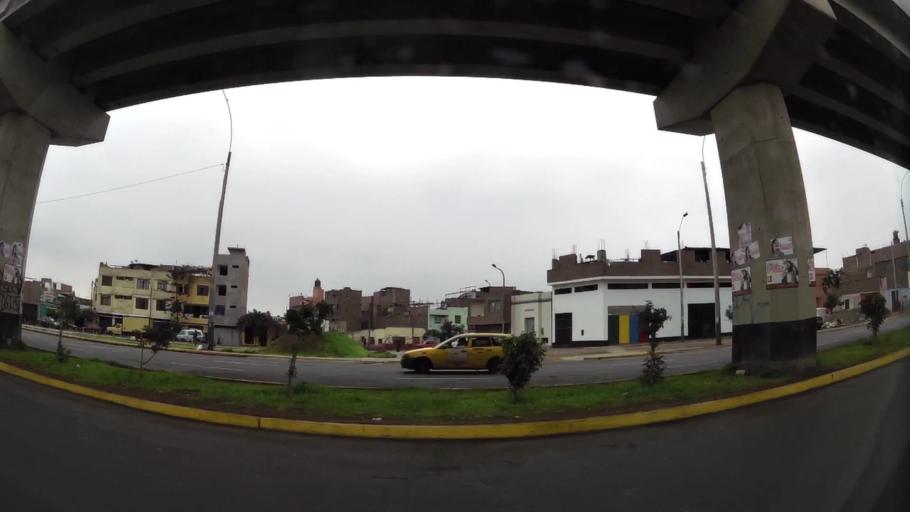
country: PE
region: Lima
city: Lima
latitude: -12.0528
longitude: -77.0116
